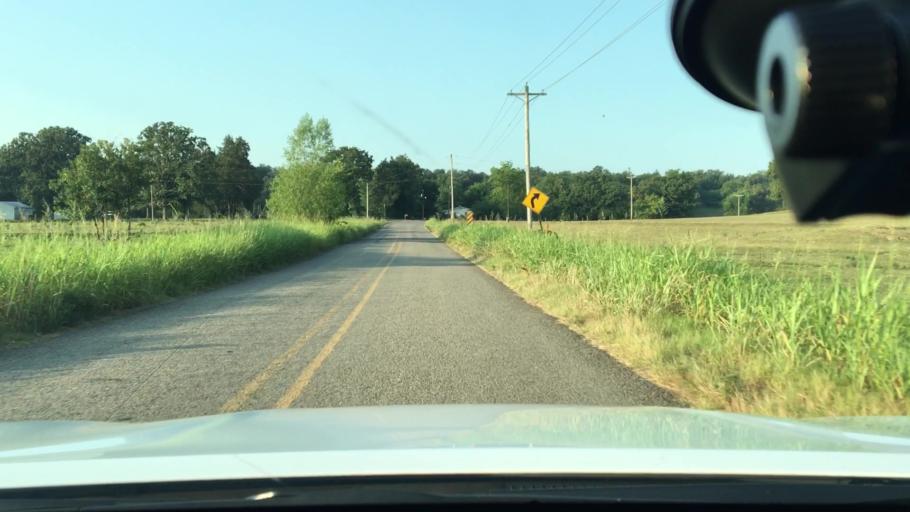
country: US
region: Arkansas
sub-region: Johnson County
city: Coal Hill
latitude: 35.3700
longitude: -93.5881
